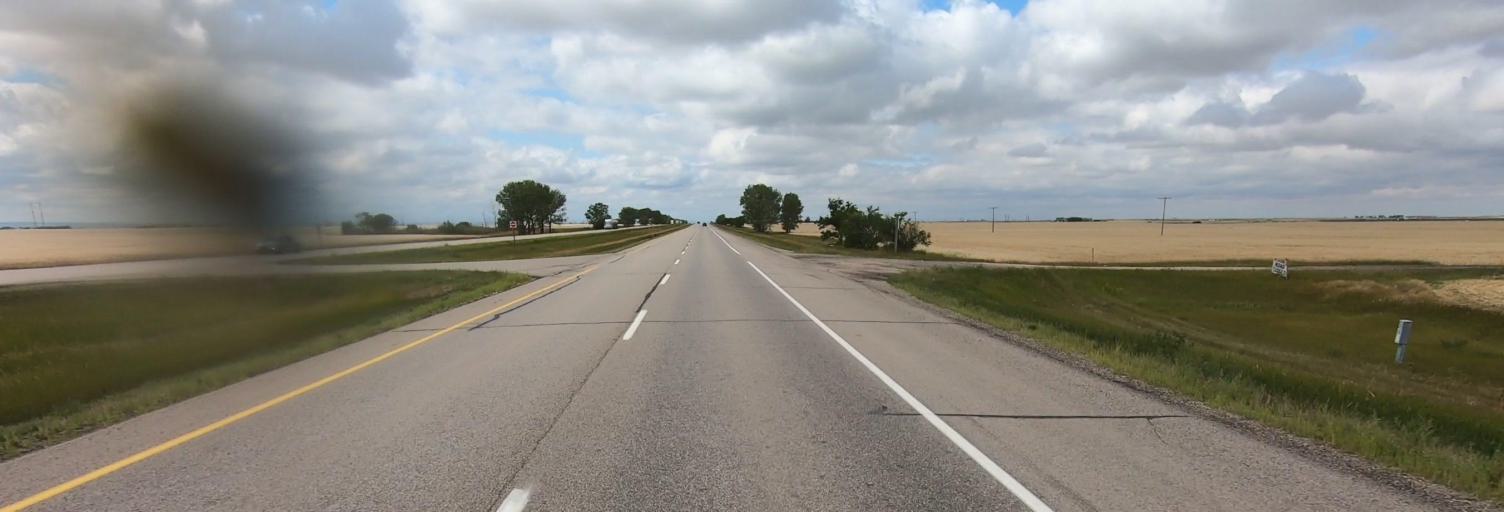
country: CA
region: Saskatchewan
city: Moose Jaw
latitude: 50.3959
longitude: -105.3268
